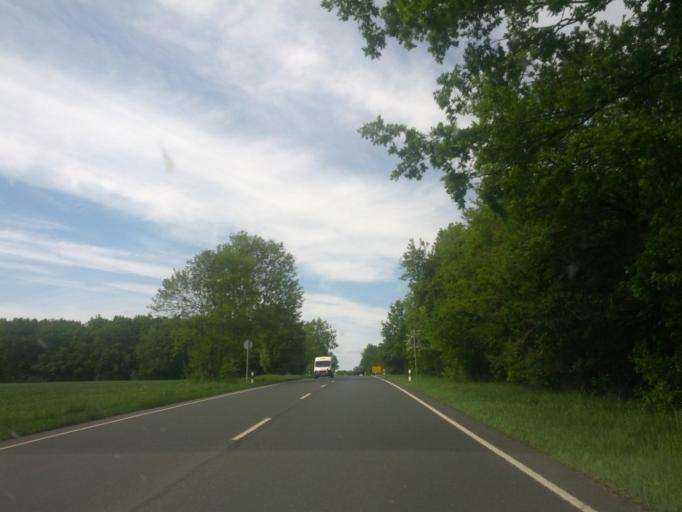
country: DE
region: Thuringia
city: Rockhausen
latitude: 50.9319
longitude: 11.0399
